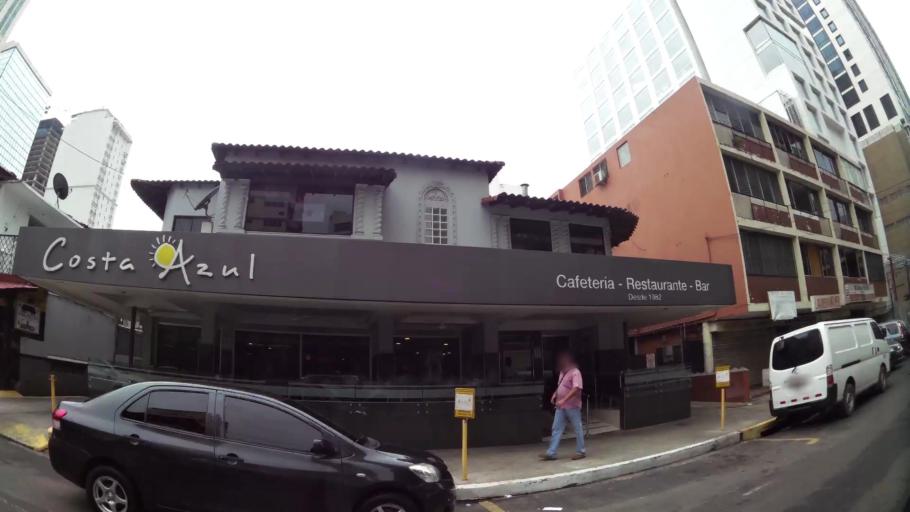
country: PA
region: Panama
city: Panama
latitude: 8.9824
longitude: -79.5247
